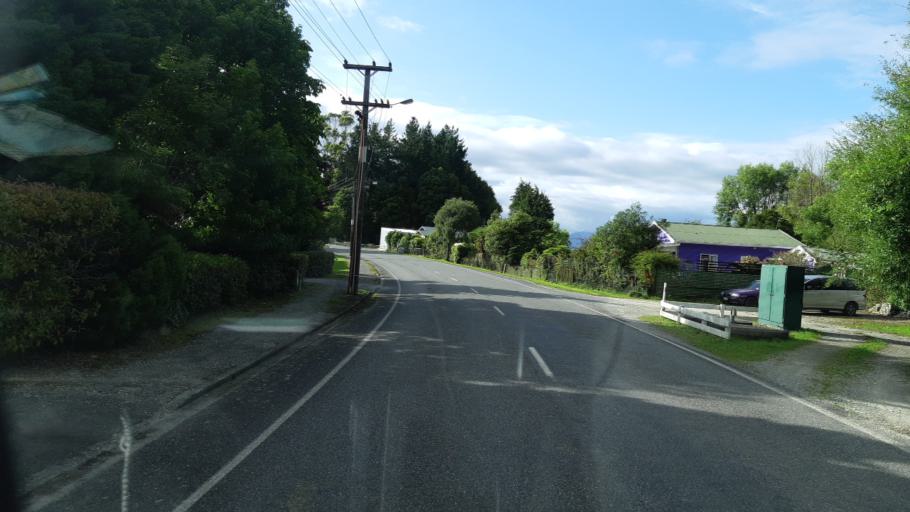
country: NZ
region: West Coast
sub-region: Westland District
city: Hokitika
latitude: -42.7458
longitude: 171.0020
